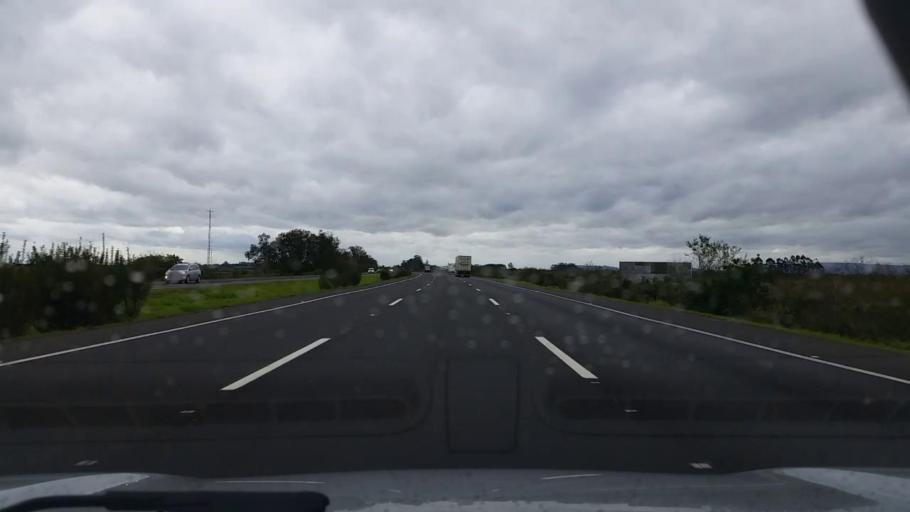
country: BR
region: Rio Grande do Sul
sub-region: Rolante
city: Rolante
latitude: -29.8863
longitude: -50.6611
